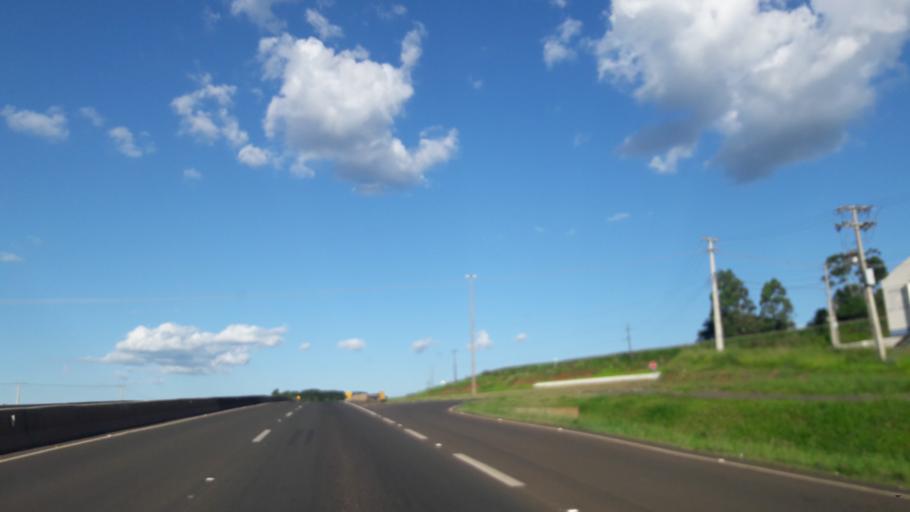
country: BR
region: Parana
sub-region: Guarapuava
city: Guarapuava
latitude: -25.3410
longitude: -51.4320
